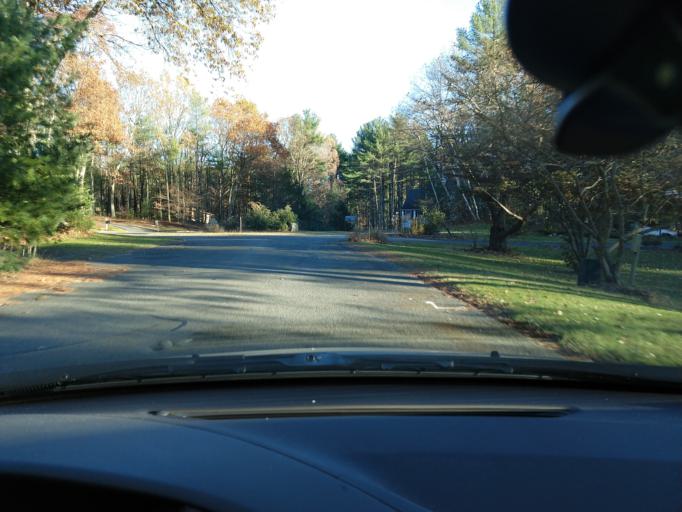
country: US
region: Massachusetts
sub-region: Middlesex County
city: Westford
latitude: 42.5384
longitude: -71.4164
